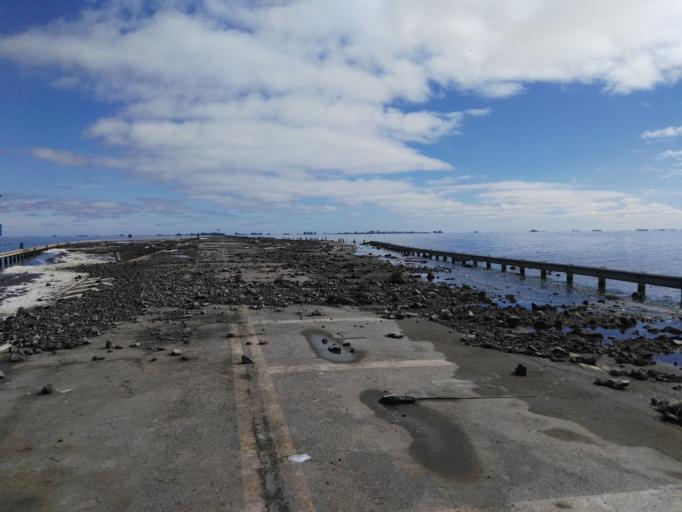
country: AR
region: Santa Fe
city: Rufino
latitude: -34.3786
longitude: -62.2911
